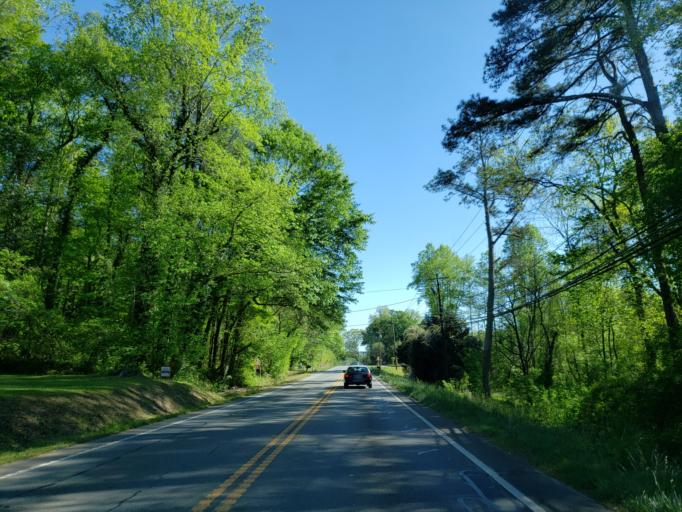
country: US
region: Georgia
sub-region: Cherokee County
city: Canton
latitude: 34.2490
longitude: -84.4940
